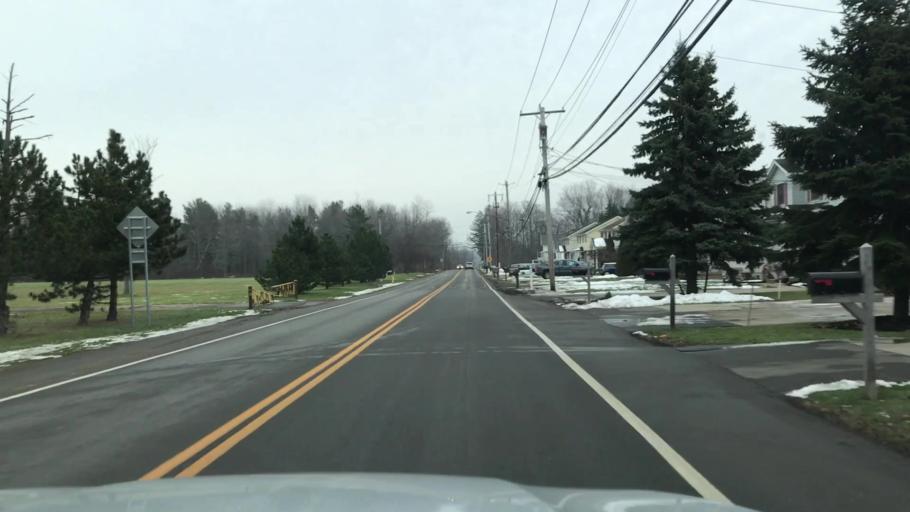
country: US
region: New York
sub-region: Erie County
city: Hamburg
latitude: 42.7515
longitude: -78.8237
